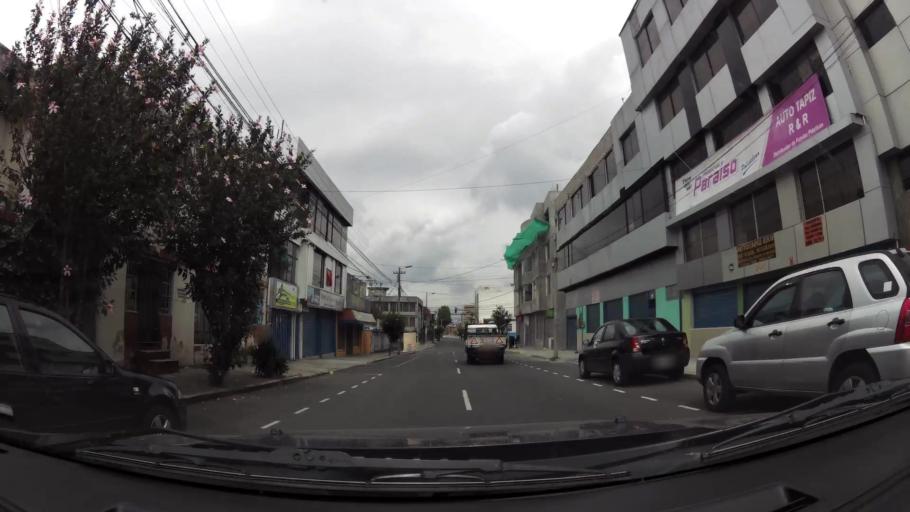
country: EC
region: Pichincha
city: Quito
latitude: -0.1922
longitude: -78.4958
